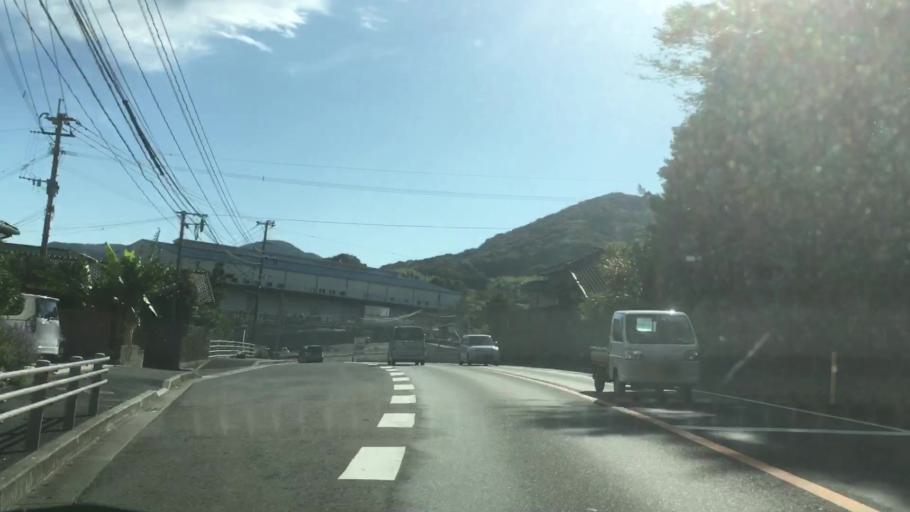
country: JP
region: Nagasaki
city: Sasebo
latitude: 33.1034
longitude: 129.7744
